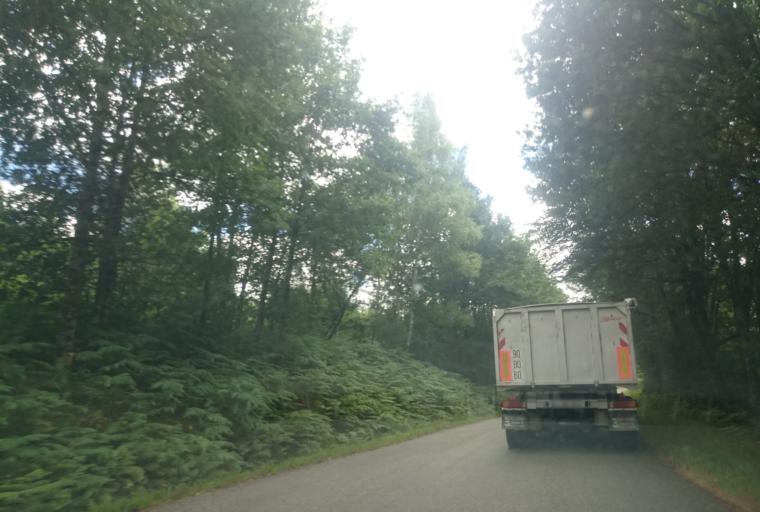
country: FR
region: Auvergne
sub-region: Departement du Cantal
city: Laroquebrou
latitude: 44.9381
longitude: 2.1976
